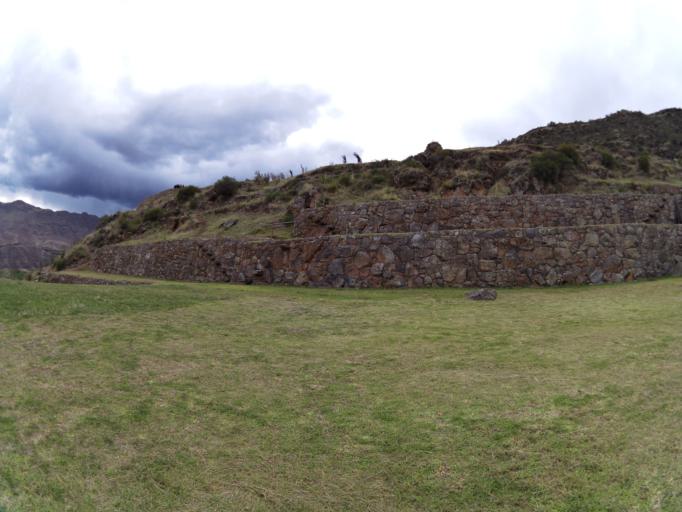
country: PE
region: Cusco
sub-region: Provincia de Quispicanchis
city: Oropesa
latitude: -13.5709
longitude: -71.7838
